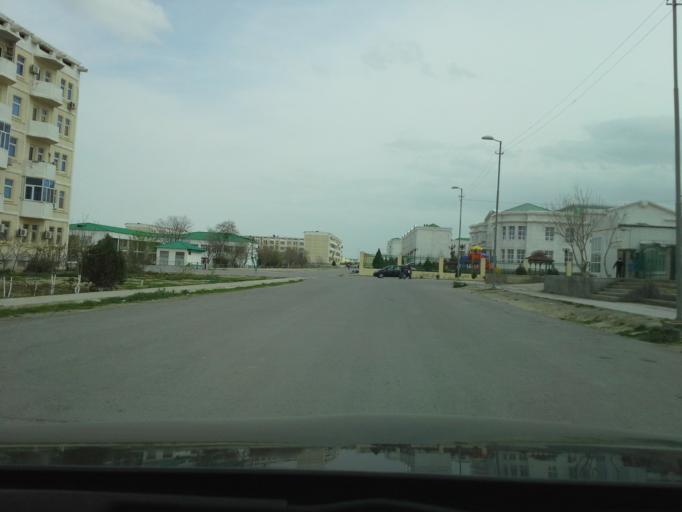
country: TM
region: Ahal
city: Abadan
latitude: 38.0539
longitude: 58.1397
